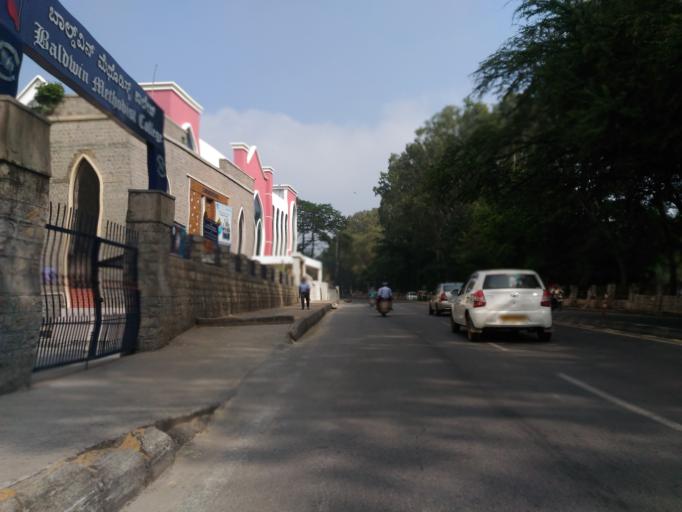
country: IN
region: Karnataka
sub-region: Bangalore Urban
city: Bangalore
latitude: 12.9615
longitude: 77.6066
